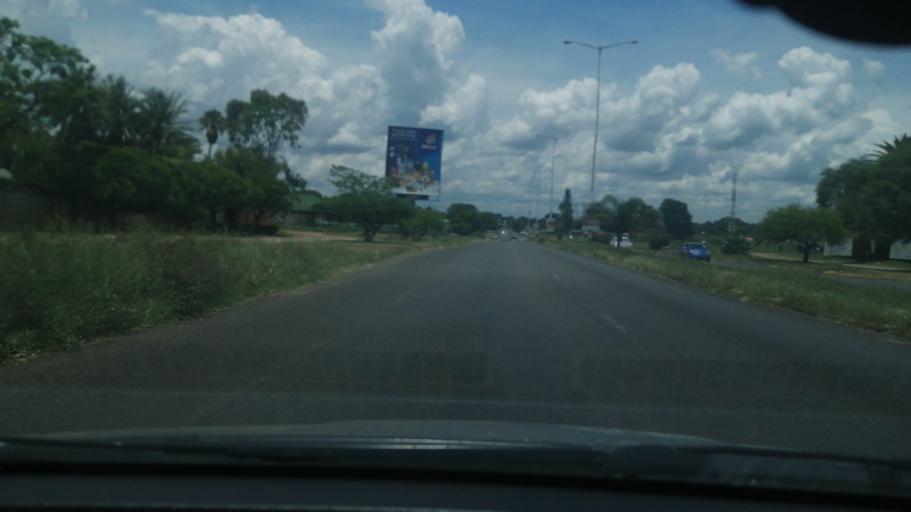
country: ZW
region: Harare
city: Harare
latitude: -17.8227
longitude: 31.0843
